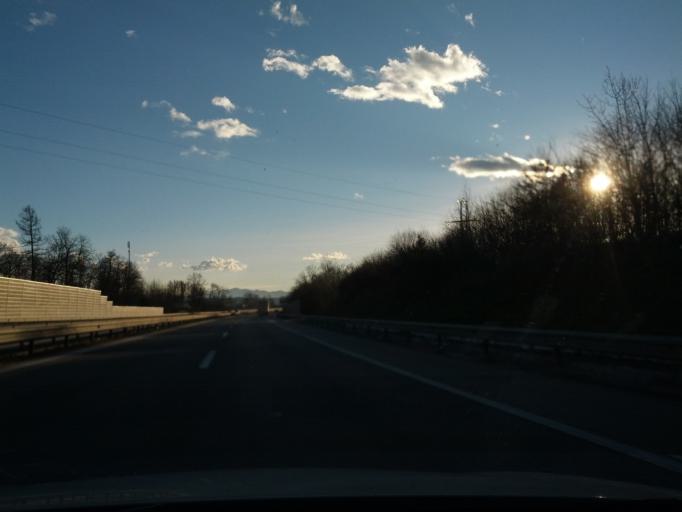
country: SI
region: Dol pri Ljubljani
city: Dol pri Ljubljani
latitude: 46.1119
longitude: 14.6012
